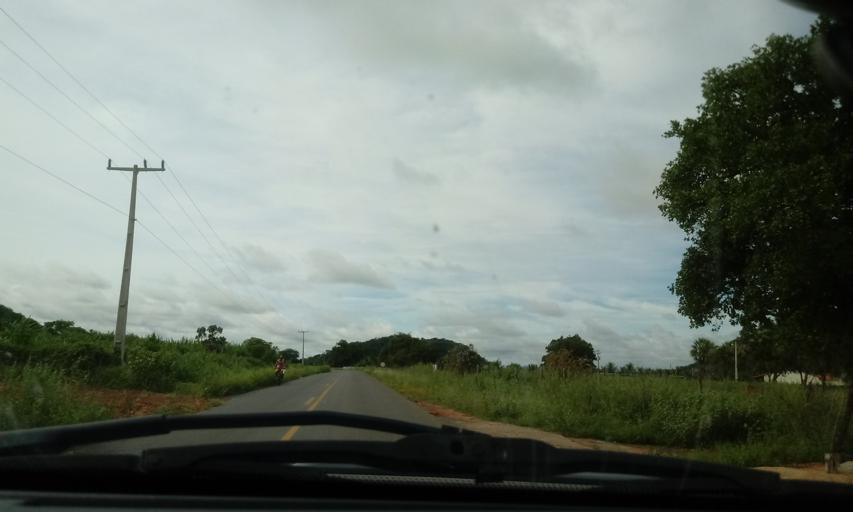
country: BR
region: Bahia
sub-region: Guanambi
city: Guanambi
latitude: -14.1293
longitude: -42.8519
